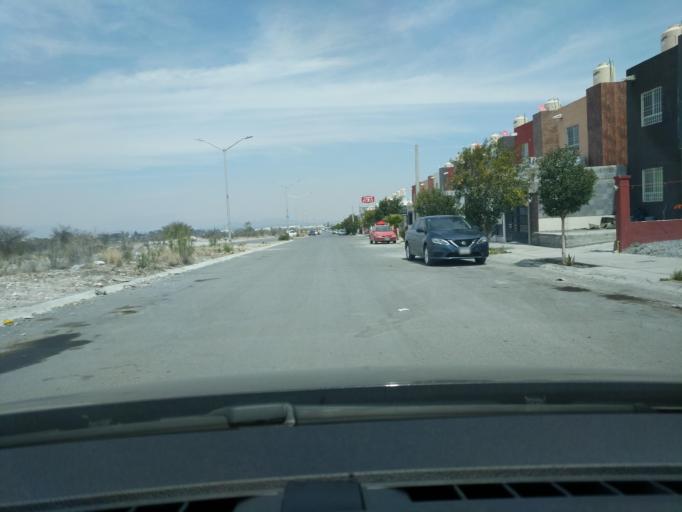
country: MX
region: Coahuila
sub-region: Arteaga
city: Arteaga
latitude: 25.4231
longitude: -100.9118
